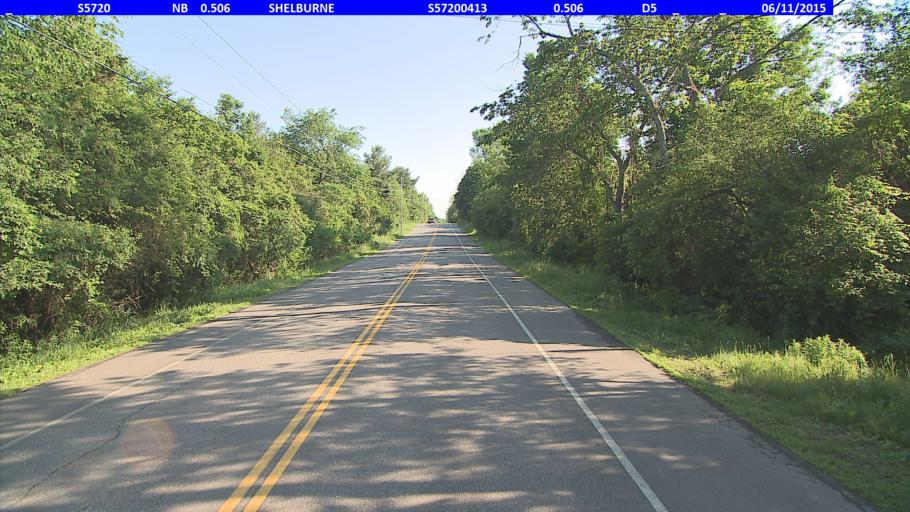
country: US
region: Vermont
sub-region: Chittenden County
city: South Burlington
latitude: 44.3754
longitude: -73.2023
